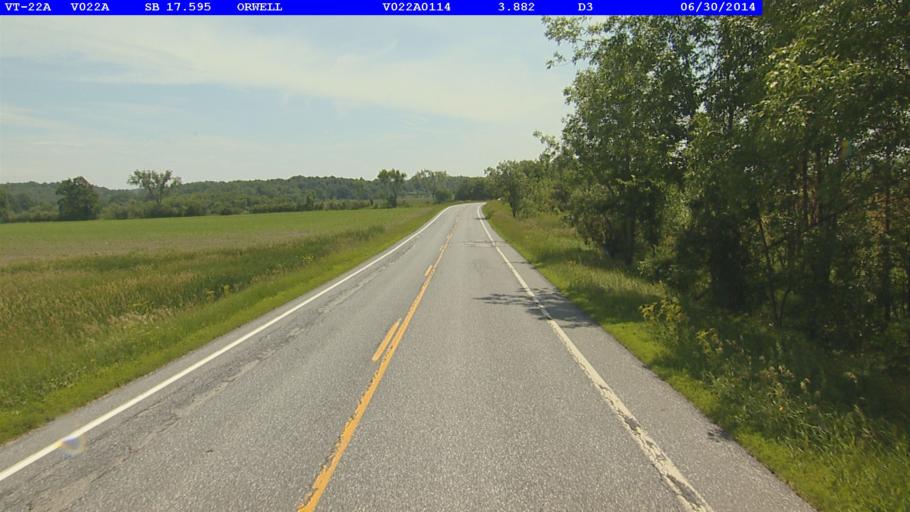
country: US
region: New York
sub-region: Essex County
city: Ticonderoga
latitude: 43.8129
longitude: -73.3047
